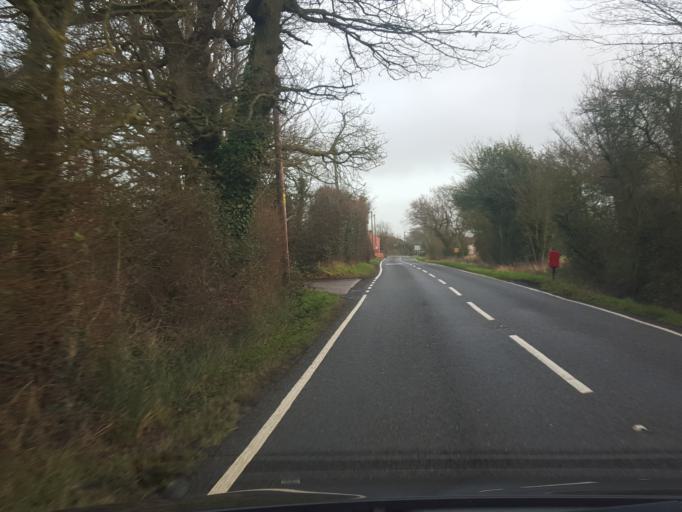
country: GB
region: England
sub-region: Essex
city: West Bergholt
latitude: 51.9488
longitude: 0.8164
